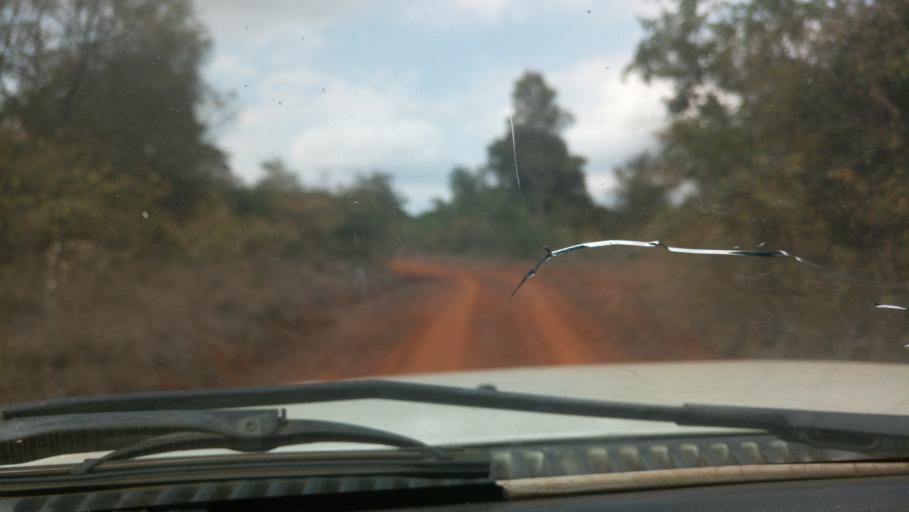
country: KE
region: Nairobi Area
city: Nairobi
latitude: -1.3625
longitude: 36.7831
